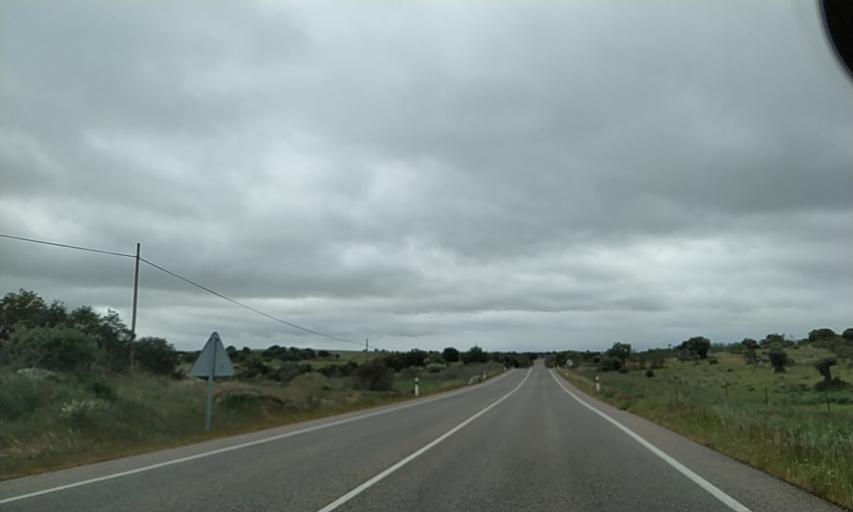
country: ES
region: Extremadura
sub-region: Provincia de Caceres
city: Caceres
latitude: 39.4197
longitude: -6.4132
